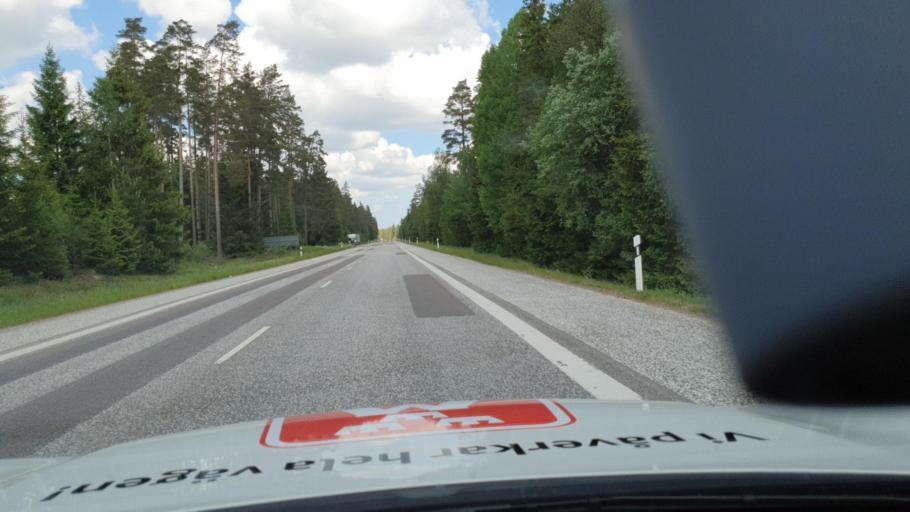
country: SE
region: Joenkoeping
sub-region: Jonkopings Kommun
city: Odensjo
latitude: 57.6275
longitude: 14.2035
